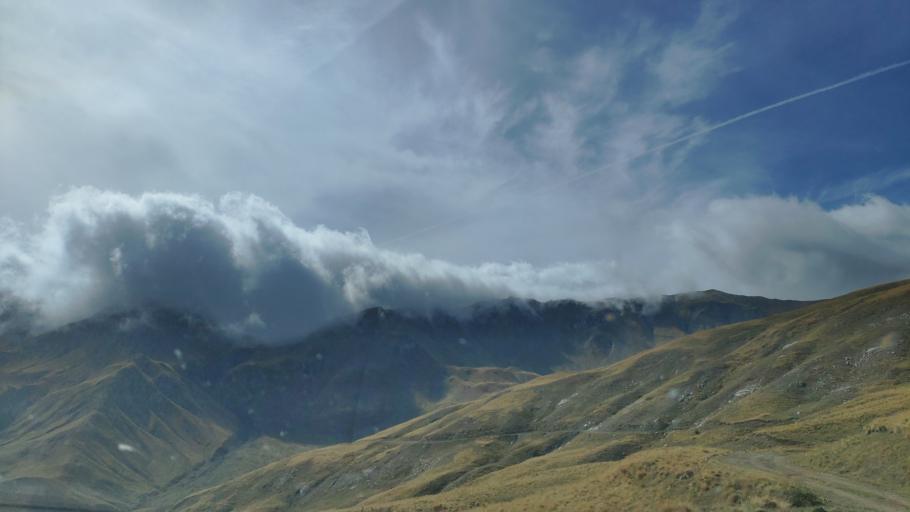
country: AL
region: Korce
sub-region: Rrethi i Kolonjes
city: Erseke
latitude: 40.3600
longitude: 20.8098
